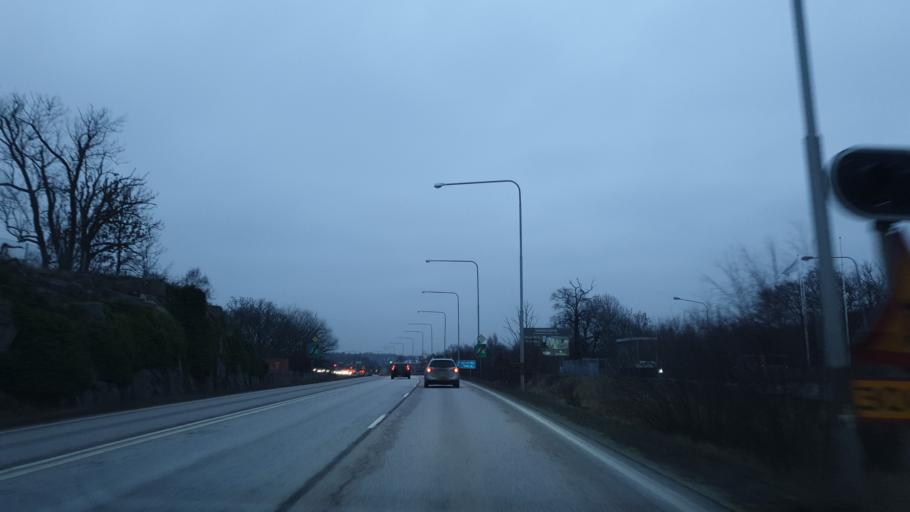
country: SE
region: Blekinge
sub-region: Karlskrona Kommun
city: Karlskrona
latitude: 56.1924
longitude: 15.6266
